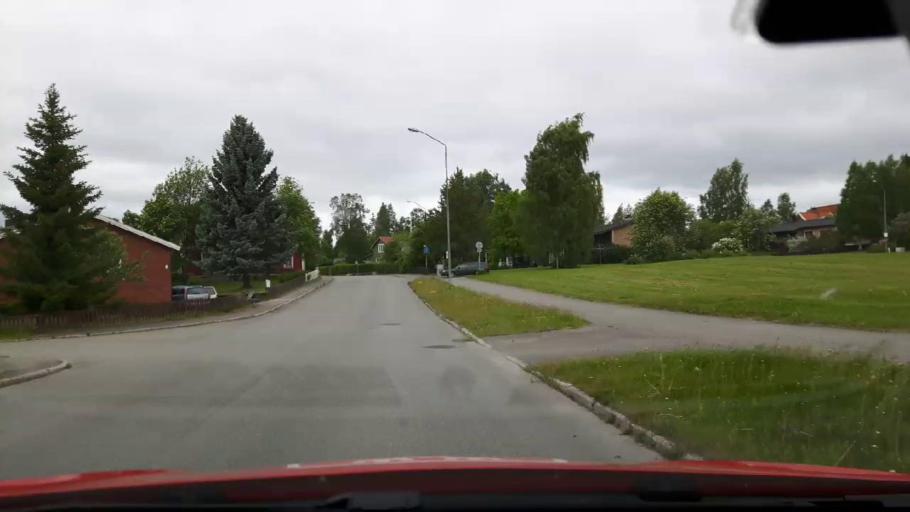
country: SE
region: Jaemtland
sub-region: OEstersunds Kommun
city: Ostersund
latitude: 63.2013
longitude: 14.6357
